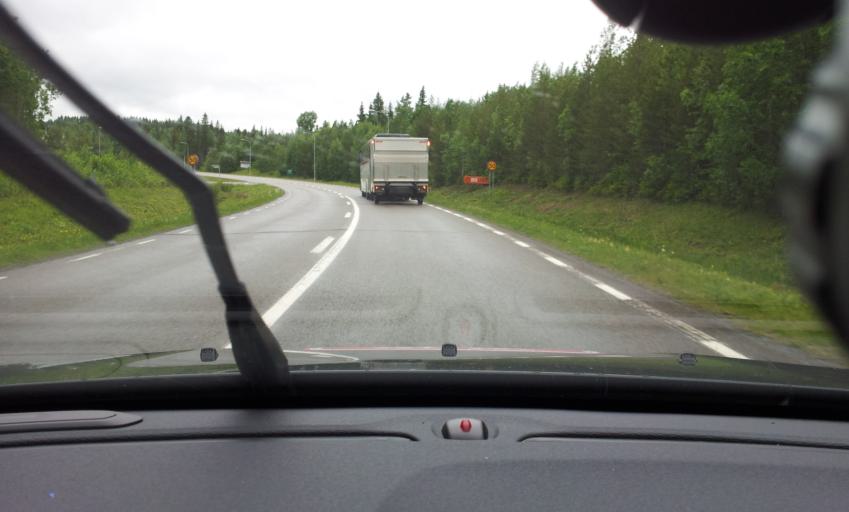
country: SE
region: Jaemtland
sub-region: Krokoms Kommun
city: Krokom
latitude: 63.6693
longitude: 14.6293
